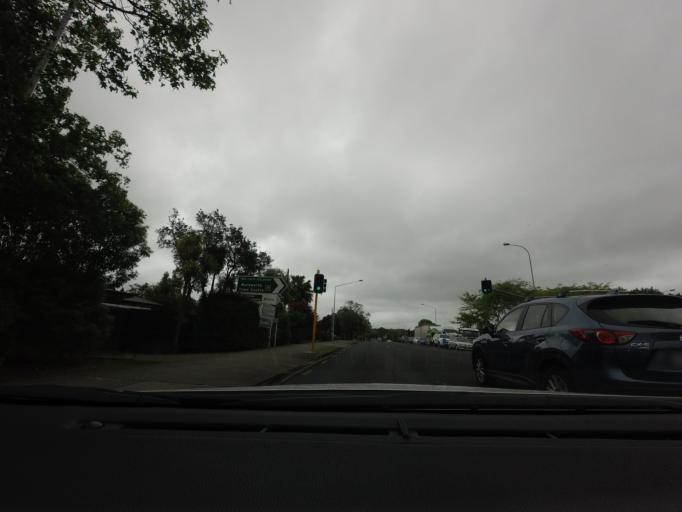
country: NZ
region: Auckland
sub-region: Auckland
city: Warkworth
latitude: -36.4025
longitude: 174.6587
